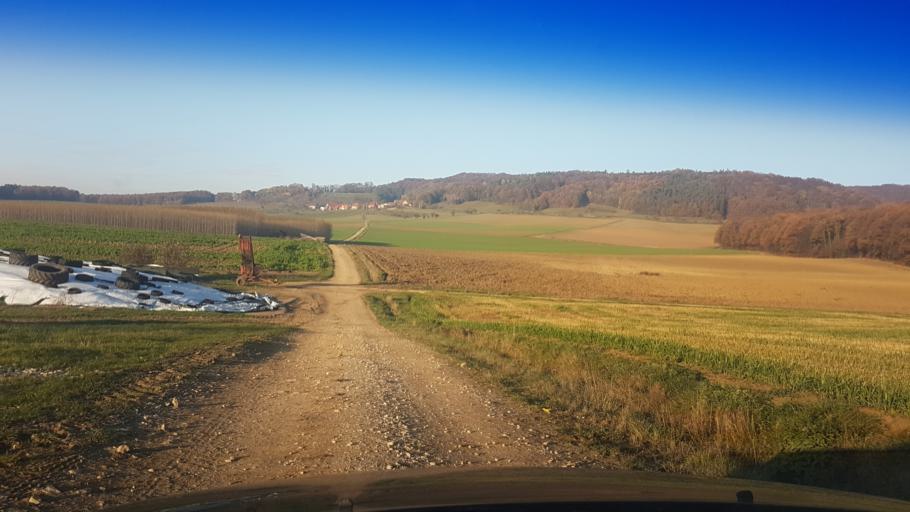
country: DE
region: Bavaria
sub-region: Upper Franconia
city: Schesslitz
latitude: 50.0038
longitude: 11.0232
